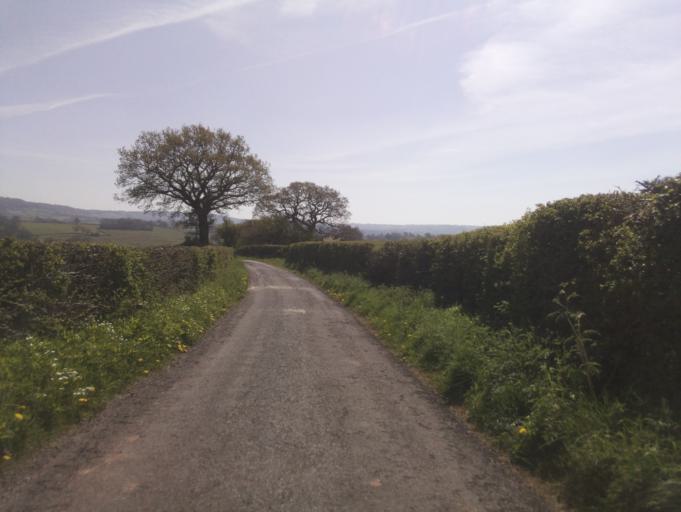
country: GB
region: Wales
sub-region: Monmouthshire
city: Llangwm
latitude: 51.7392
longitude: -2.8233
